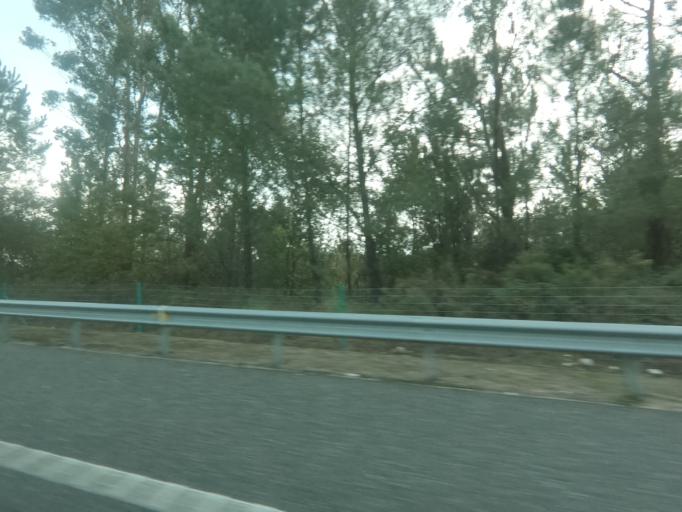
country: ES
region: Galicia
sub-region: Provincia de Pontevedra
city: Tui
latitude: 42.0726
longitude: -8.6394
